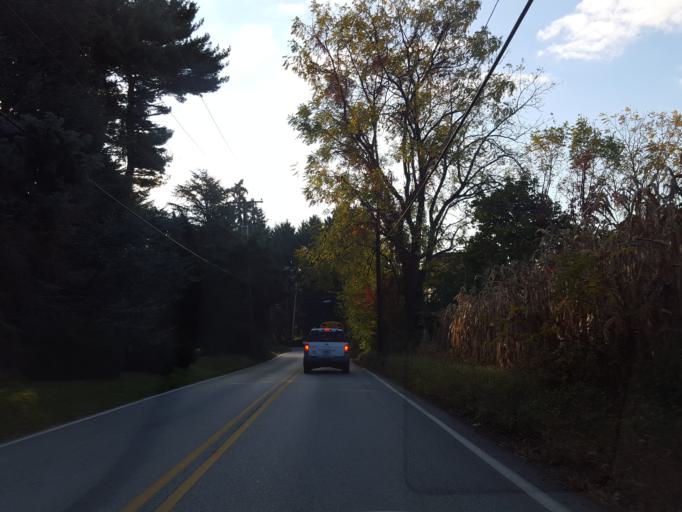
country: US
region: Pennsylvania
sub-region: York County
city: Stonybrook
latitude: 39.9625
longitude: -76.6312
